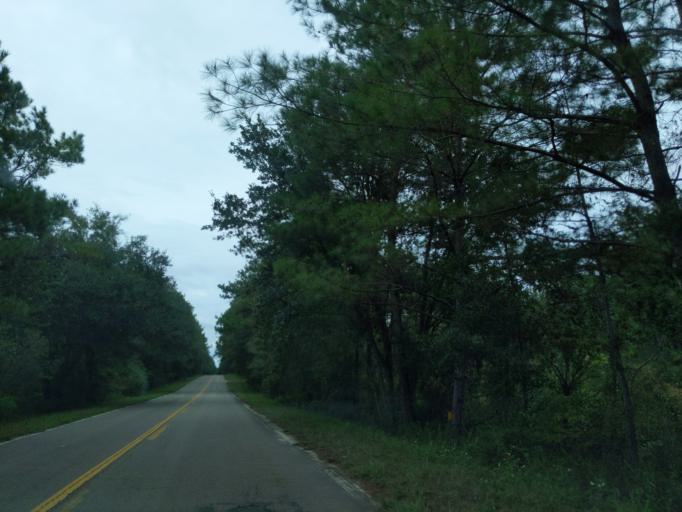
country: US
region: Florida
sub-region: Leon County
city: Woodville
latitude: 30.3700
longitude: -84.1470
